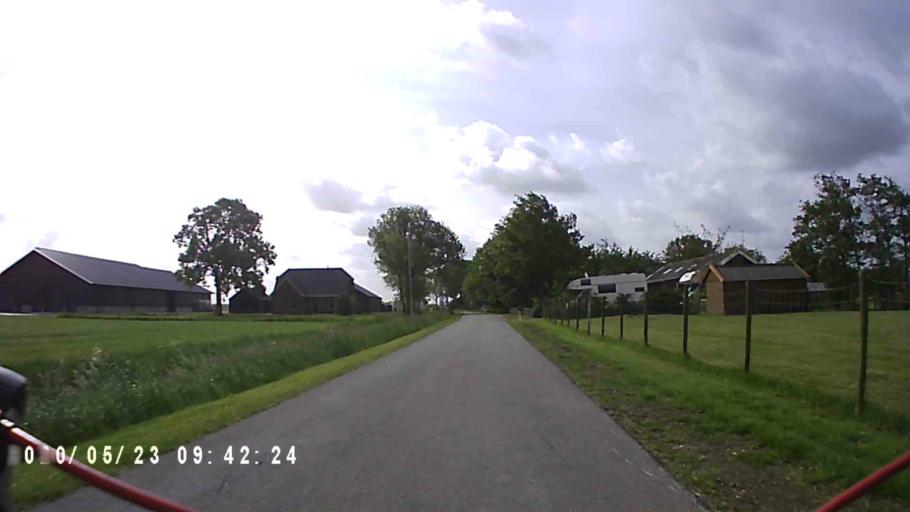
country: NL
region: Groningen
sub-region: Gemeente Slochteren
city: Slochteren
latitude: 53.2896
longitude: 6.7457
